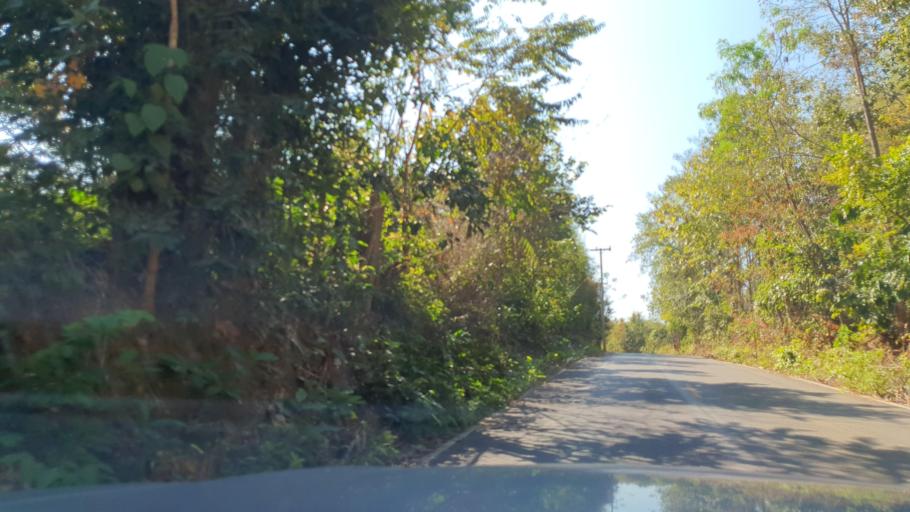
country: TH
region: Nan
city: Pua
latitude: 19.1692
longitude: 100.9094
